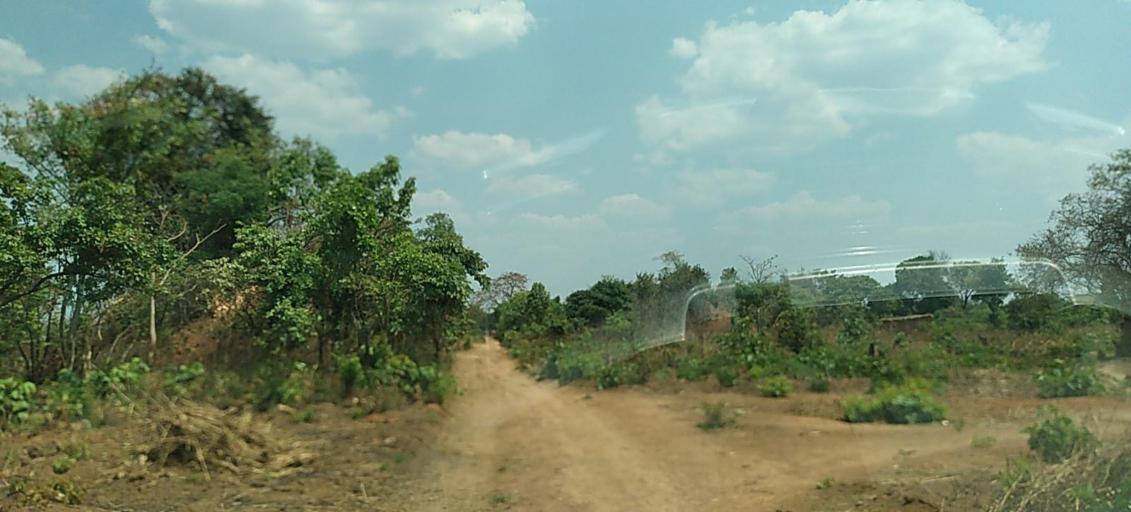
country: CD
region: Katanga
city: Kipushi
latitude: -12.0223
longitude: 27.4344
